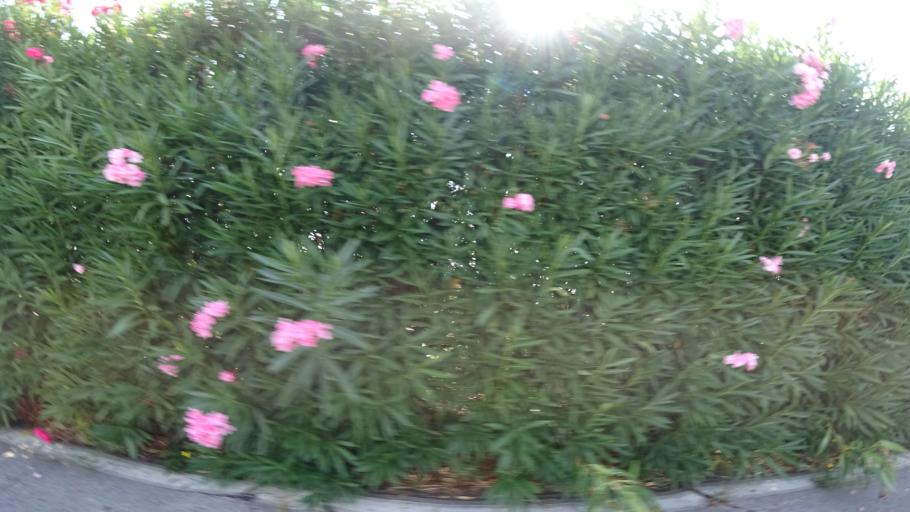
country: FR
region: Languedoc-Roussillon
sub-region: Departement des Pyrenees-Orientales
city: Bompas
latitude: 42.7193
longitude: 2.9324
